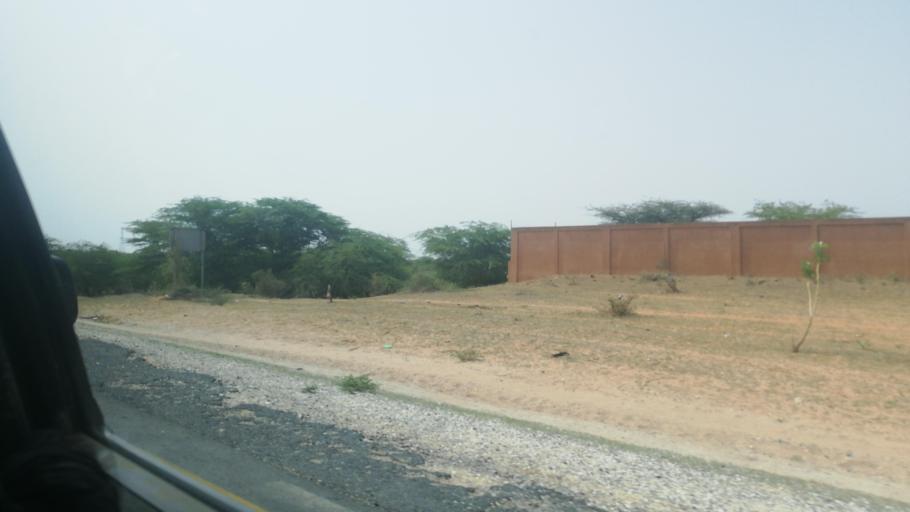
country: SN
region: Saint-Louis
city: Saint-Louis
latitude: 16.0765
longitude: -16.3790
